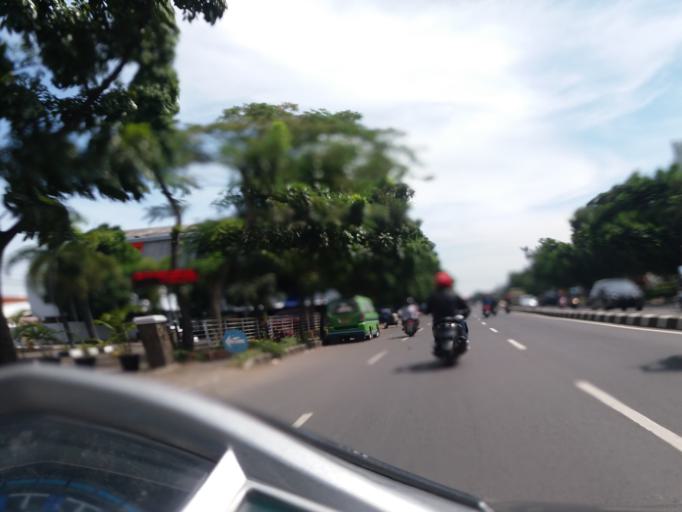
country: ID
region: West Java
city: Bandung
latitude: -6.9495
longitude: 107.6241
